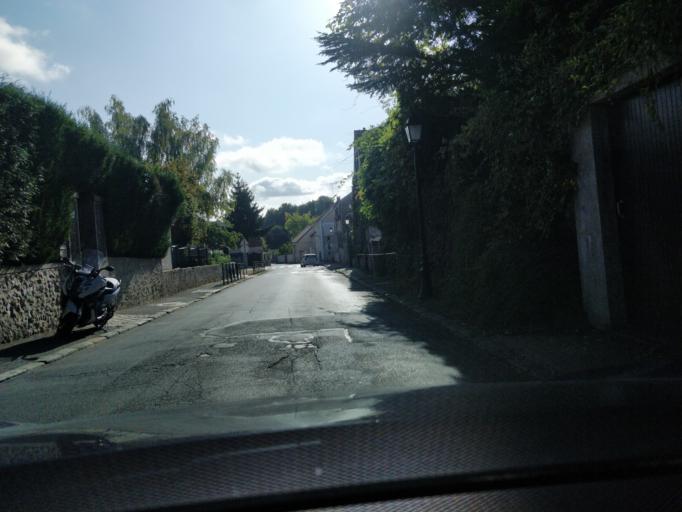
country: FR
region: Ile-de-France
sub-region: Departement de l'Essonne
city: Vaugrigneuse
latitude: 48.6026
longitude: 2.1201
